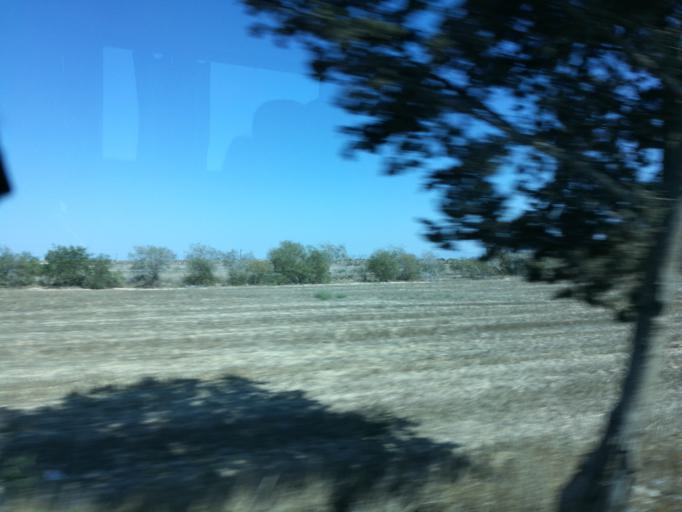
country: CY
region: Ammochostos
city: Acheritou
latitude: 35.0751
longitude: 33.8647
